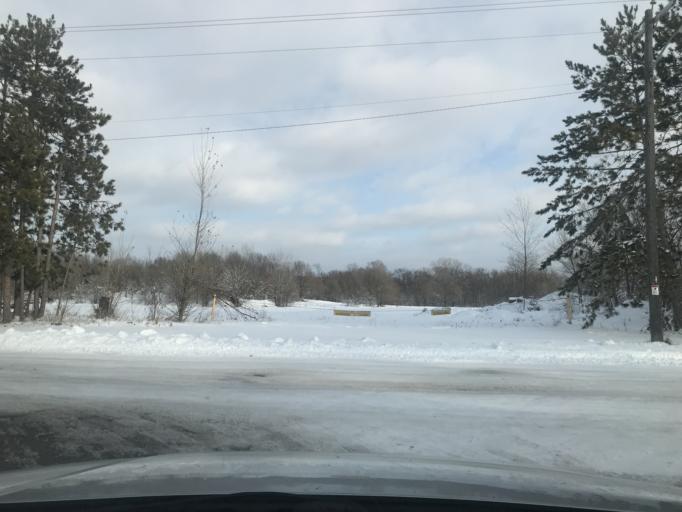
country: US
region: Wisconsin
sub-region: Marinette County
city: Peshtigo
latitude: 45.0487
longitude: -87.7489
